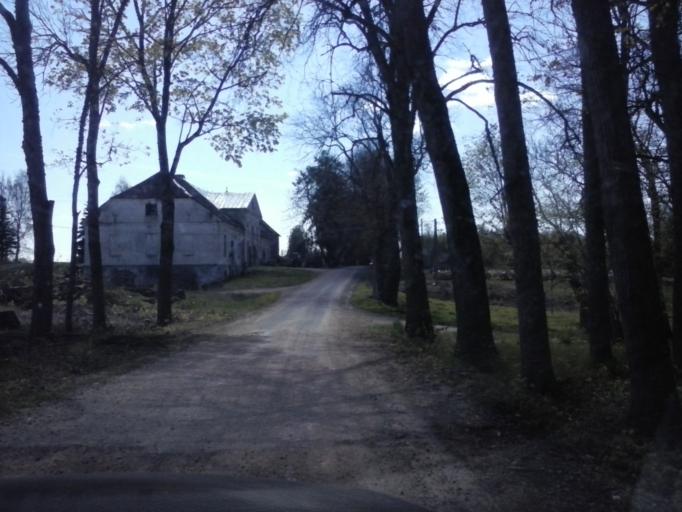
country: EE
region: Valgamaa
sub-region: Torva linn
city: Torva
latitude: 58.2325
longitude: 25.8910
